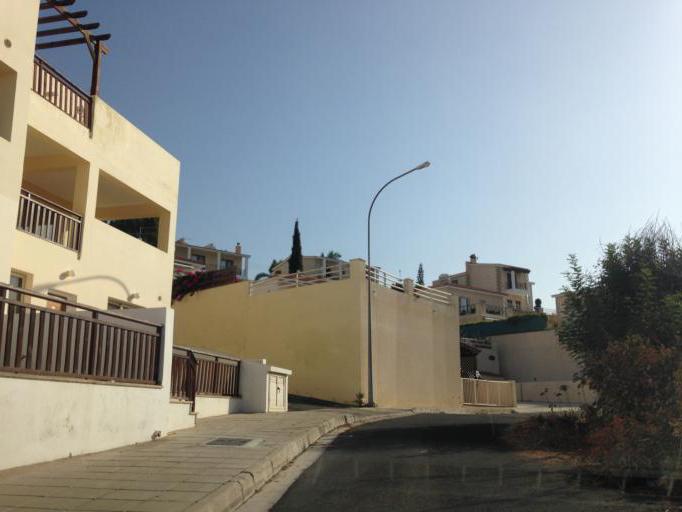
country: CY
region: Pafos
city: Pegeia
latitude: 34.8826
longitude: 32.3884
